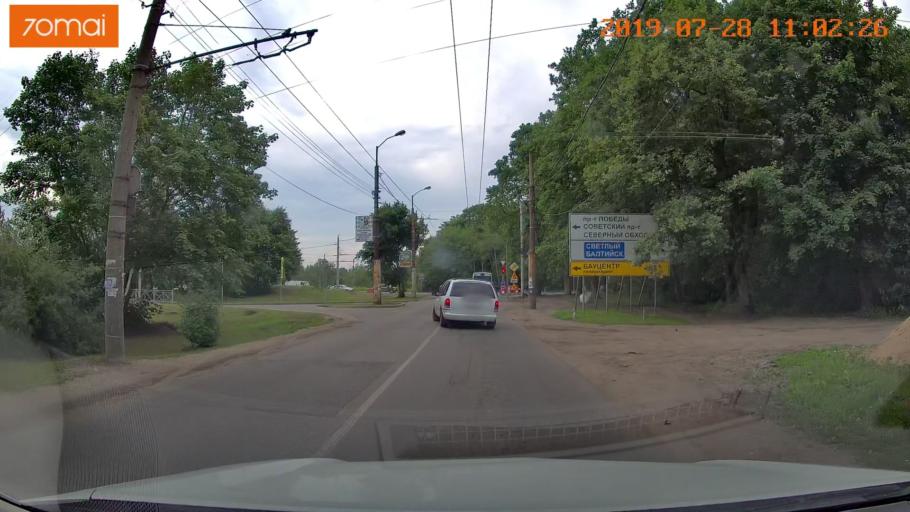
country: RU
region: Kaliningrad
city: Vzmorye
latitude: 54.7158
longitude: 20.3708
